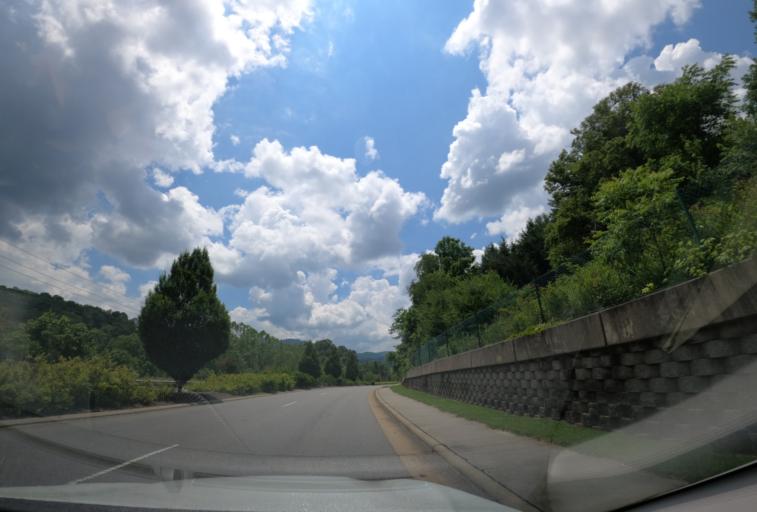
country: US
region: North Carolina
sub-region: Haywood County
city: Lake Junaluska
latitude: 35.5033
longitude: -82.9636
